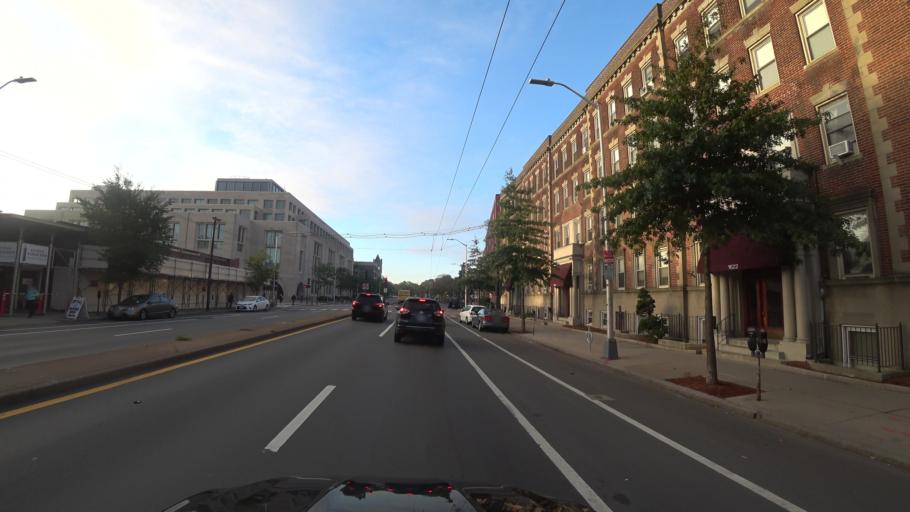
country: US
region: Massachusetts
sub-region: Middlesex County
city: Cambridge
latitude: 42.3809
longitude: -71.1199
